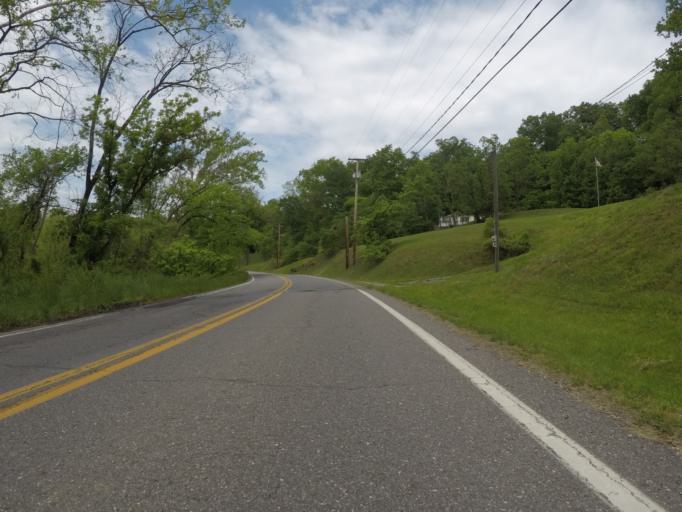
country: US
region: West Virginia
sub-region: Wayne County
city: Ceredo
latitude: 38.3551
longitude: -82.5353
